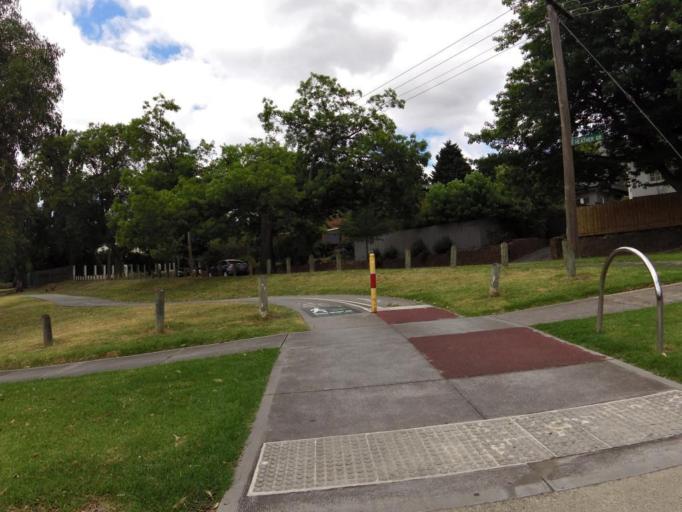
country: AU
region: Victoria
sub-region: Boroondara
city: Kew East
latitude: -37.8044
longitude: 145.0598
